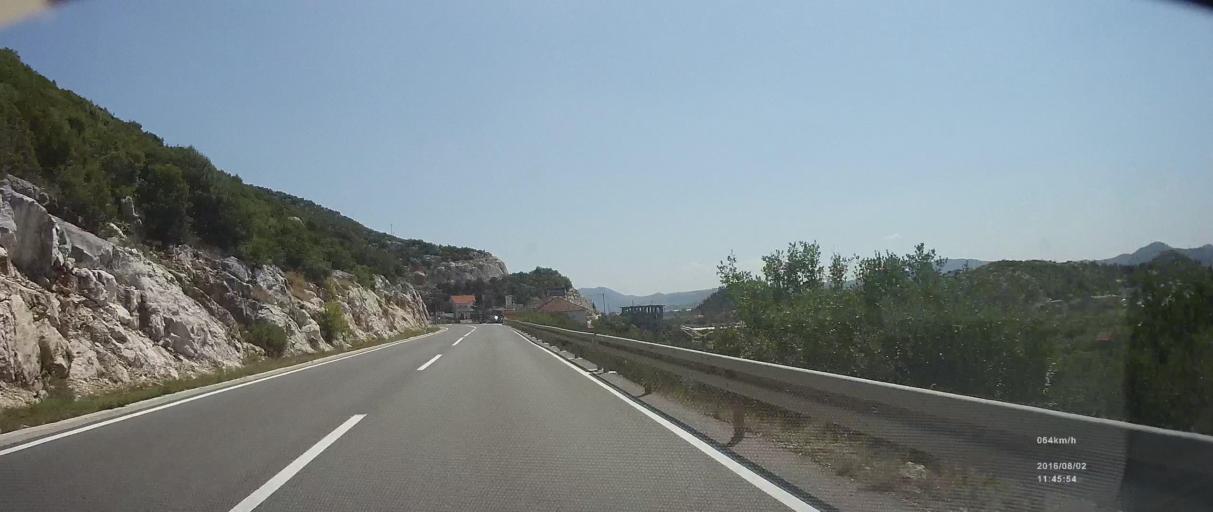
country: HR
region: Dubrovacko-Neretvanska
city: Komin
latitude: 43.0538
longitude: 17.4705
